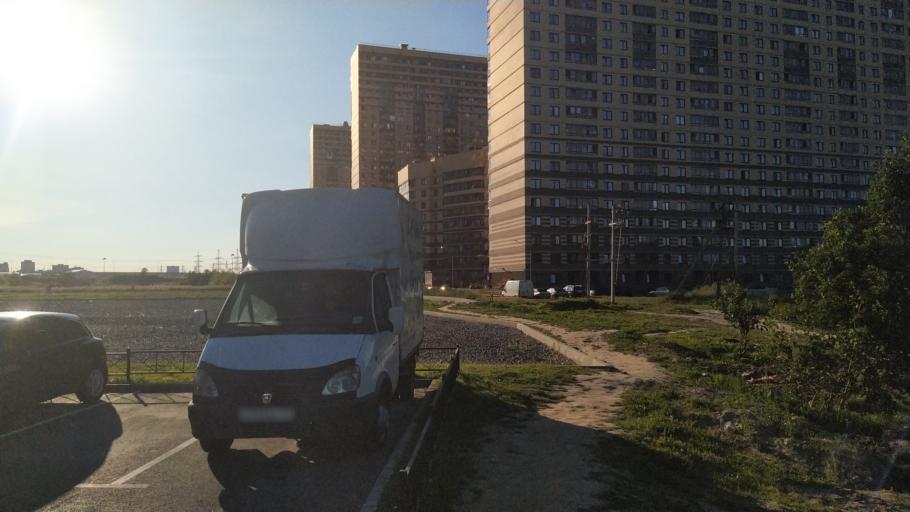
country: RU
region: Leningrad
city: Murino
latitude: 60.0373
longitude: 30.4580
